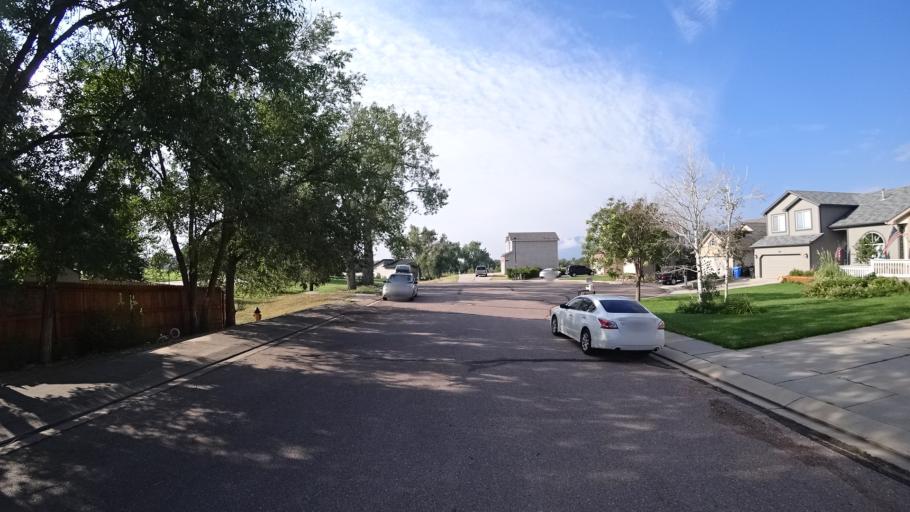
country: US
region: Colorado
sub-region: El Paso County
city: Colorado Springs
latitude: 38.8845
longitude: -104.8034
